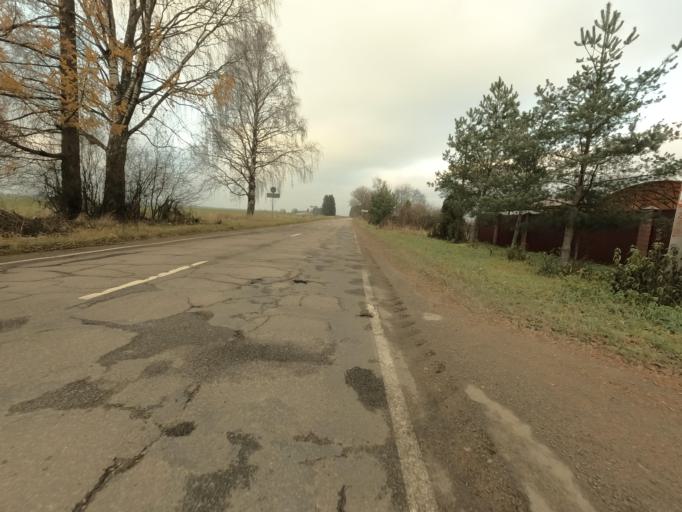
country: RU
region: Leningrad
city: Mga
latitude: 59.7764
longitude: 31.0244
